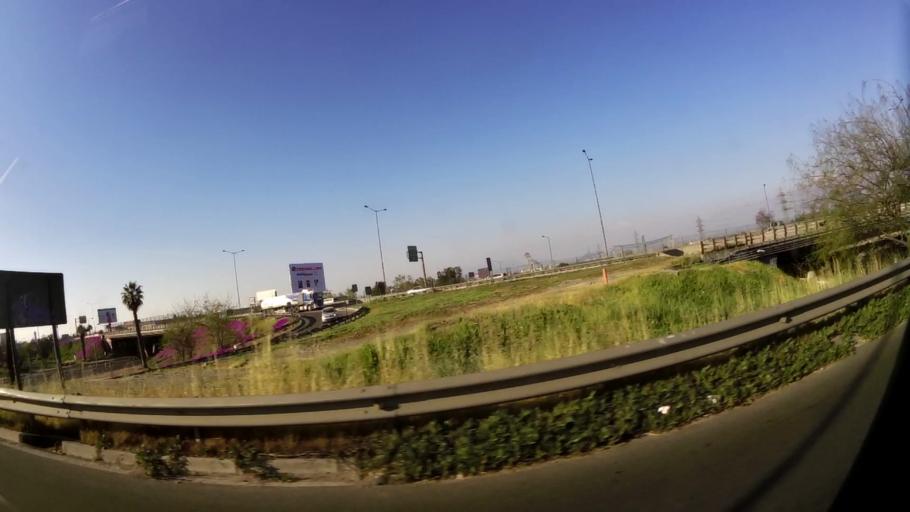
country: CL
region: Santiago Metropolitan
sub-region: Provincia de Santiago
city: Lo Prado
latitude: -33.4891
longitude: -70.7507
